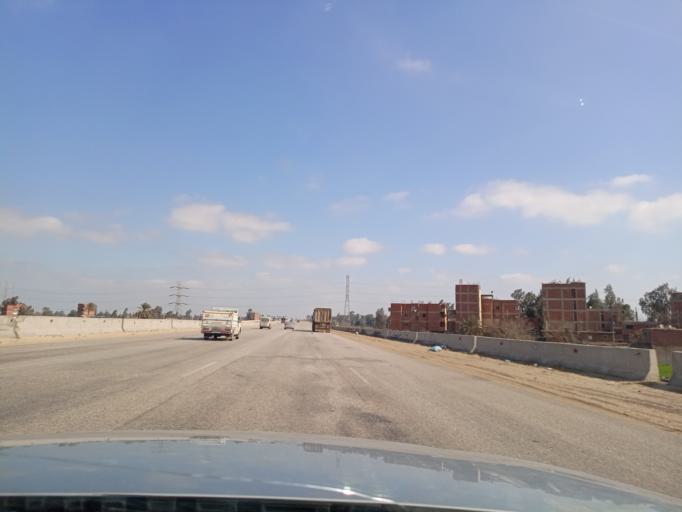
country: EG
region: Muhafazat al Minufiyah
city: Al Bajur
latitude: 30.4374
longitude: 31.1084
